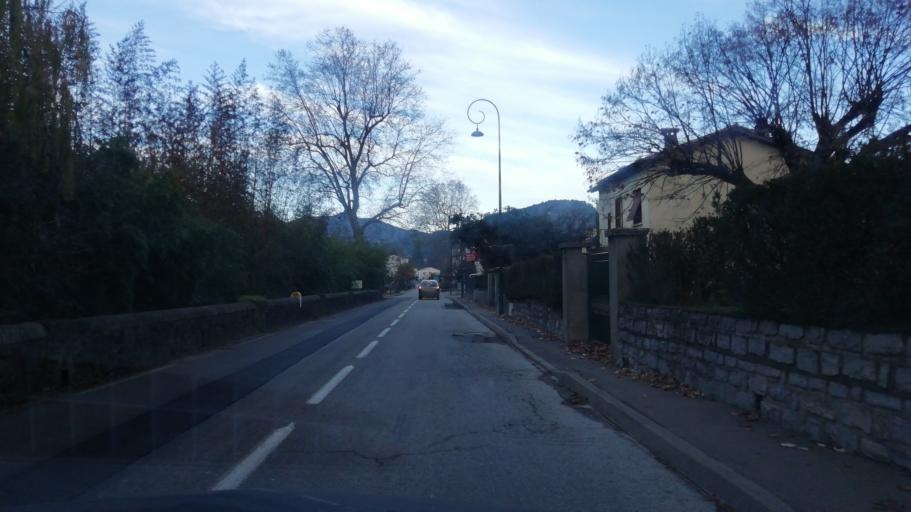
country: FR
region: Languedoc-Roussillon
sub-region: Departement du Gard
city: Lasalle
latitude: 44.0415
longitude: 3.8619
